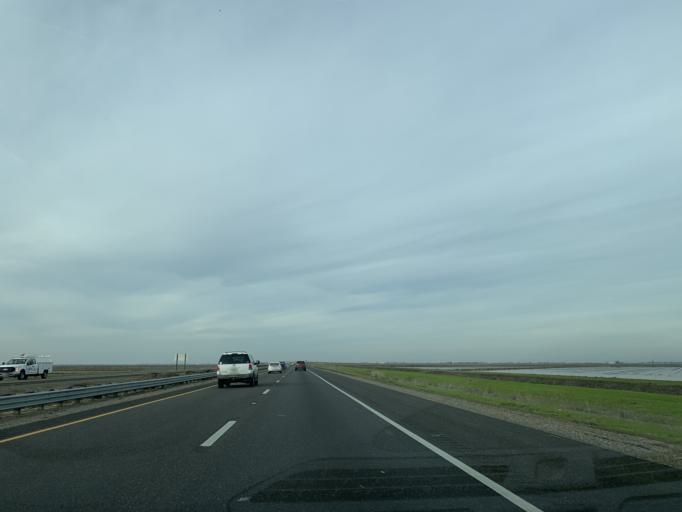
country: US
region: California
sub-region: Sacramento County
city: Elverta
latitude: 38.7299
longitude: -121.5403
